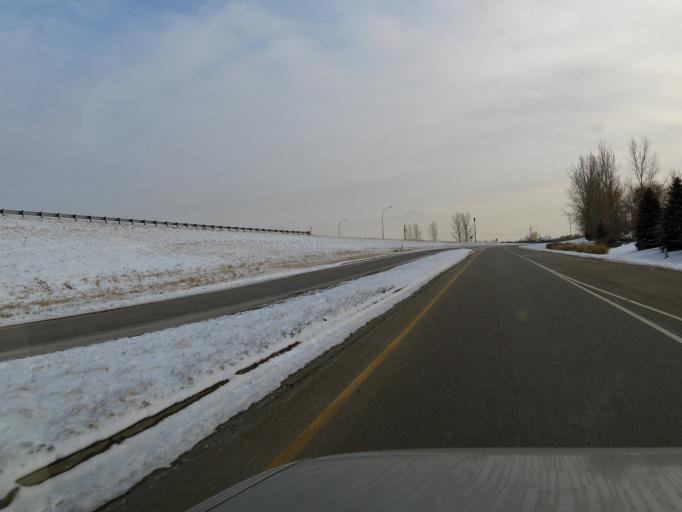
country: US
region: Minnesota
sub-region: Scott County
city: Shakopee
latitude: 44.7462
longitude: -93.5014
